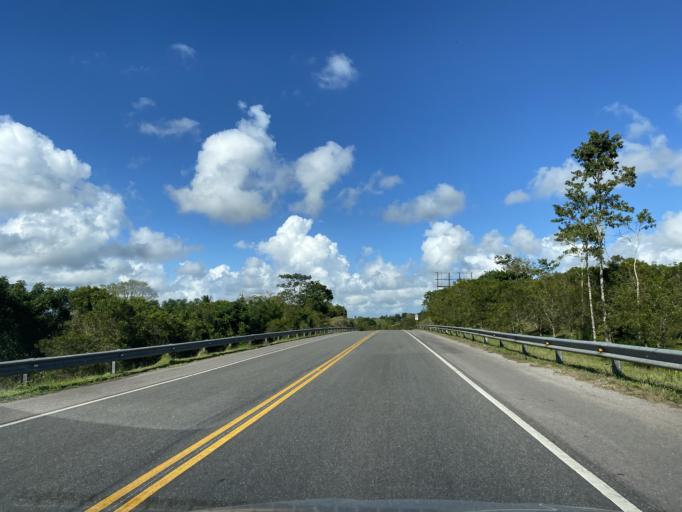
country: DO
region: Monte Plata
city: Majagual
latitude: 19.0208
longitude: -69.8226
